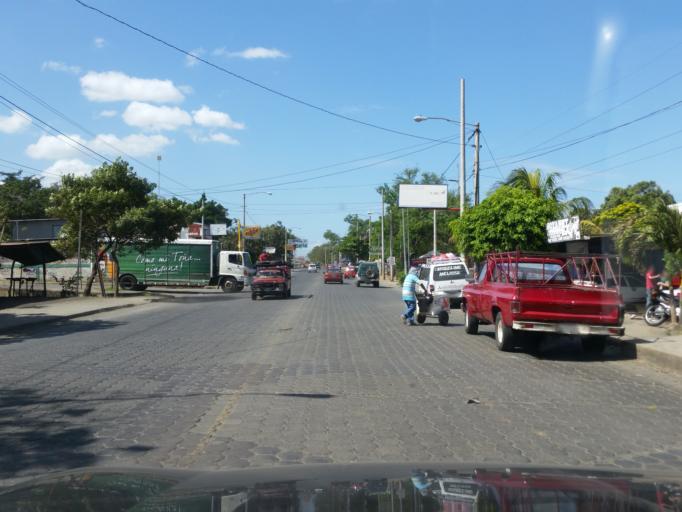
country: NI
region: Managua
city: Managua
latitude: 12.1275
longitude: -86.2101
